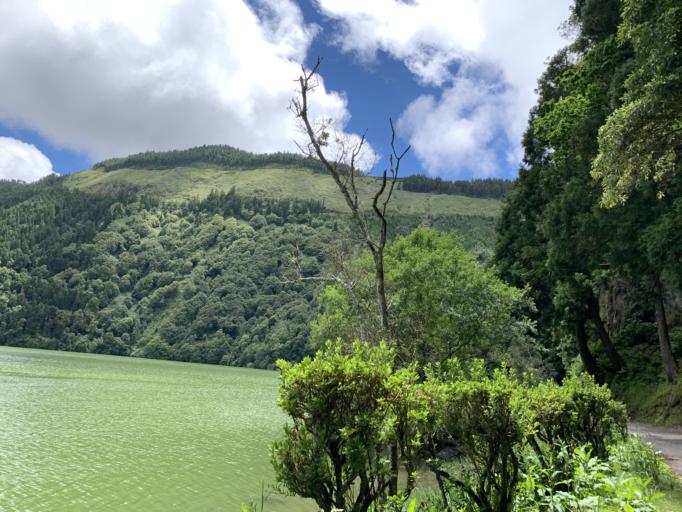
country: PT
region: Azores
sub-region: Ponta Delgada
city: Arrifes
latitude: 37.8461
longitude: -25.7942
